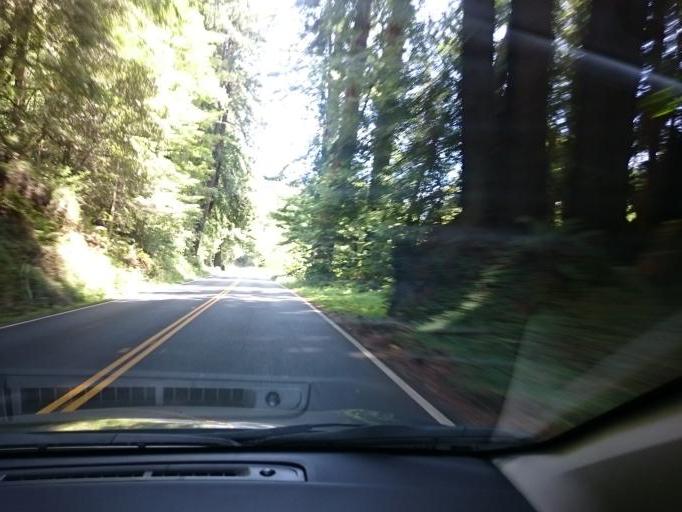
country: US
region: California
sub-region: Mendocino County
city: Fort Bragg
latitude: 39.1780
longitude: -123.6866
